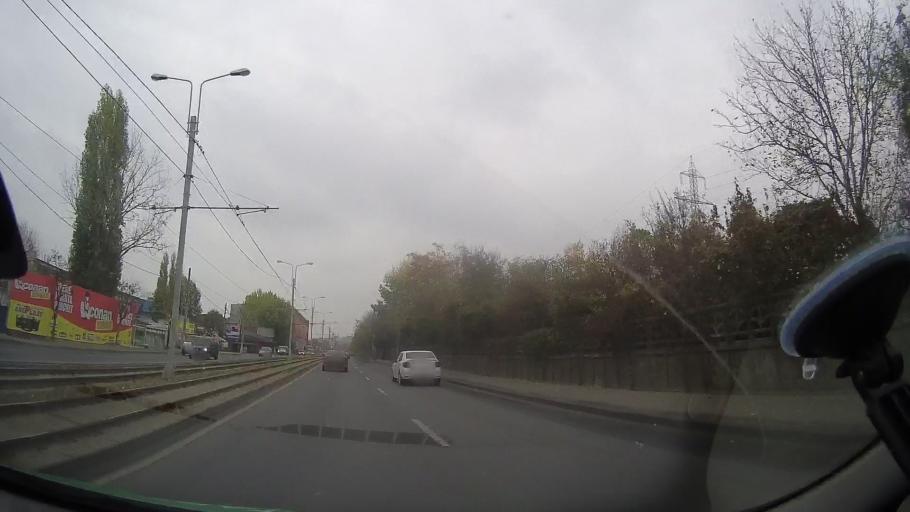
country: RO
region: Ilfov
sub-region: Comuna Chiajna
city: Rosu
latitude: 44.4241
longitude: 26.0053
